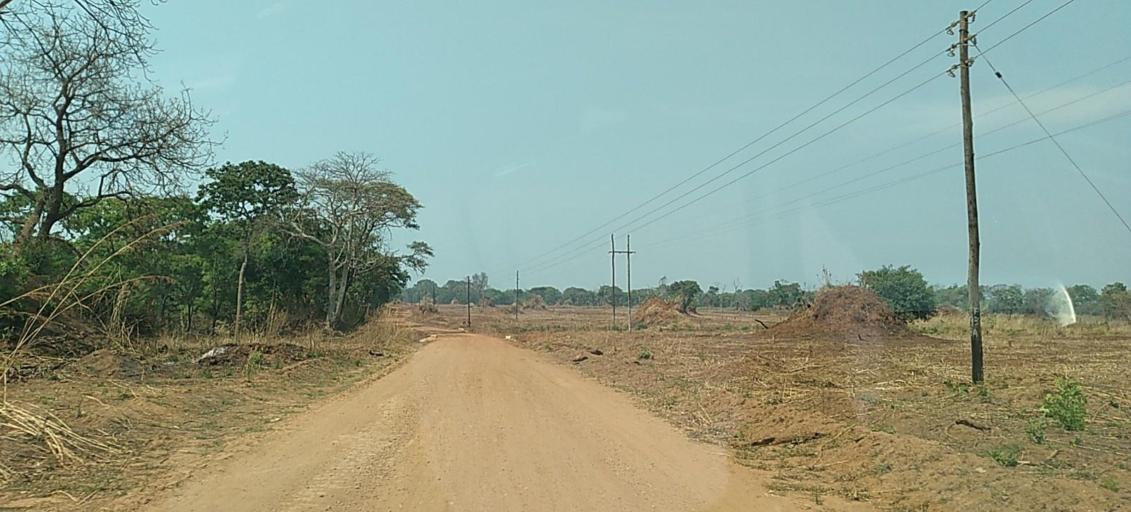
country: ZM
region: Copperbelt
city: Chingola
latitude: -13.0644
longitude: 27.4177
